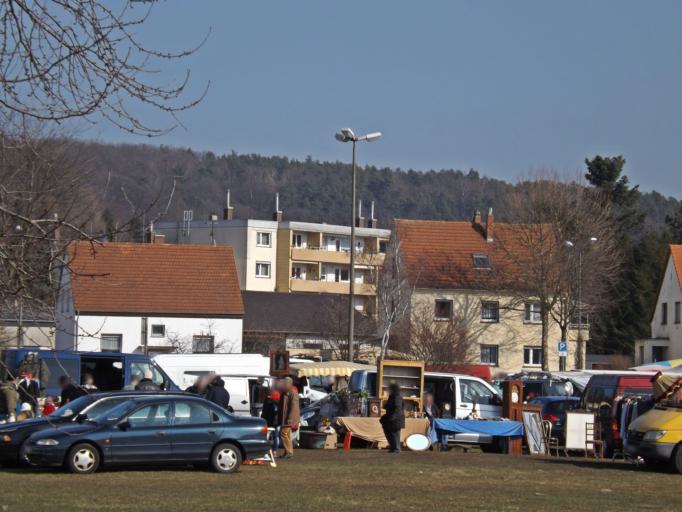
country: DE
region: Saarland
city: Homburg
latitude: 49.3167
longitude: 7.3336
